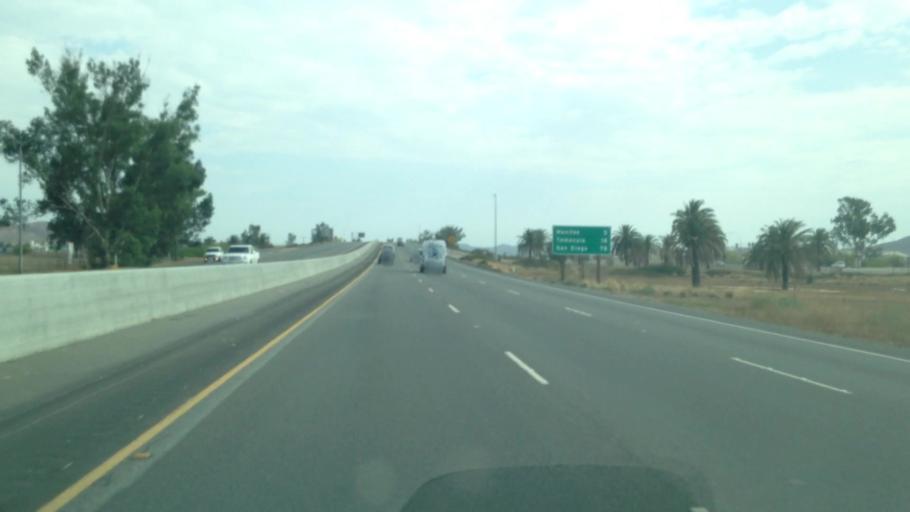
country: US
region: California
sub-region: Riverside County
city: Romoland
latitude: 33.7589
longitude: -117.1893
